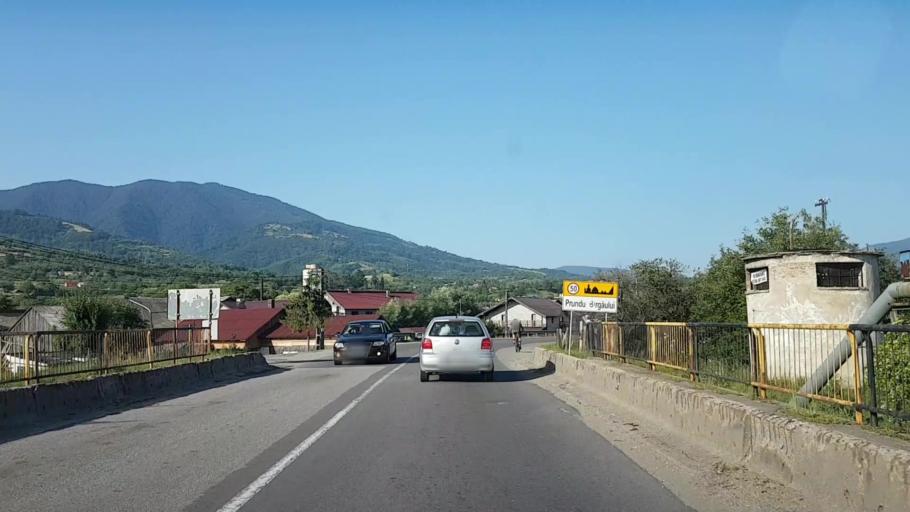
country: RO
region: Bistrita-Nasaud
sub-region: Comuna Prundu Bargaului
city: Susenii Bargaului
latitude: 47.2201
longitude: 24.7207
